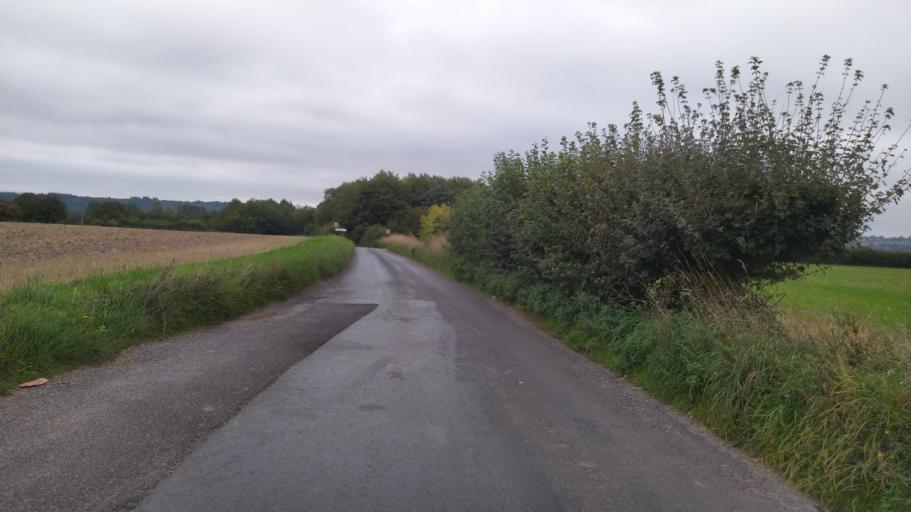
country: GB
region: England
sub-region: Hampshire
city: Long Sutton
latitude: 51.1963
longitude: -0.8826
